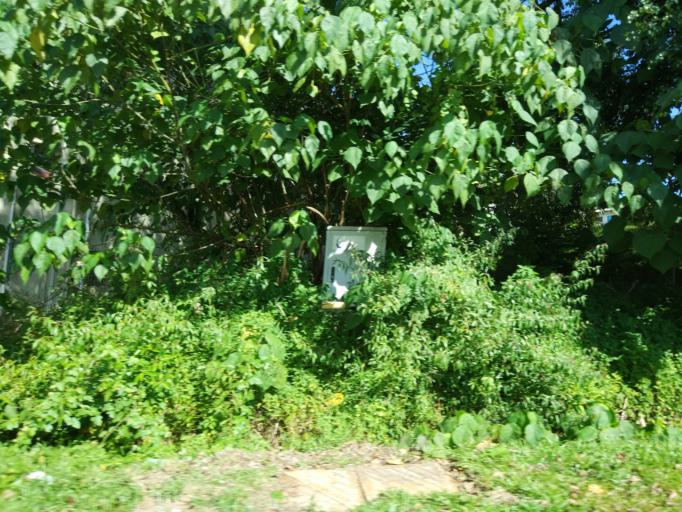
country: BN
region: Brunei and Muara
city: Bandar Seri Begawan
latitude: 4.8743
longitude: 114.9555
